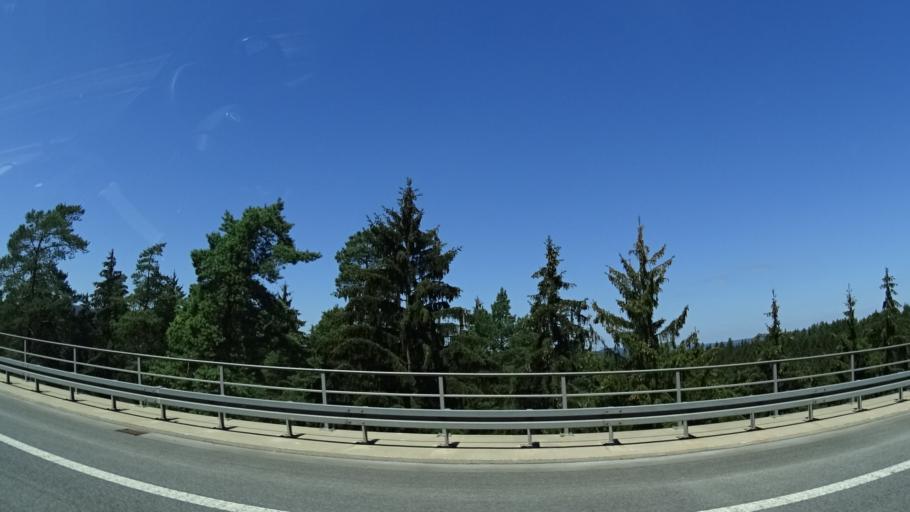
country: DE
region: Thuringia
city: Schwarza
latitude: 50.6111
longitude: 10.5616
